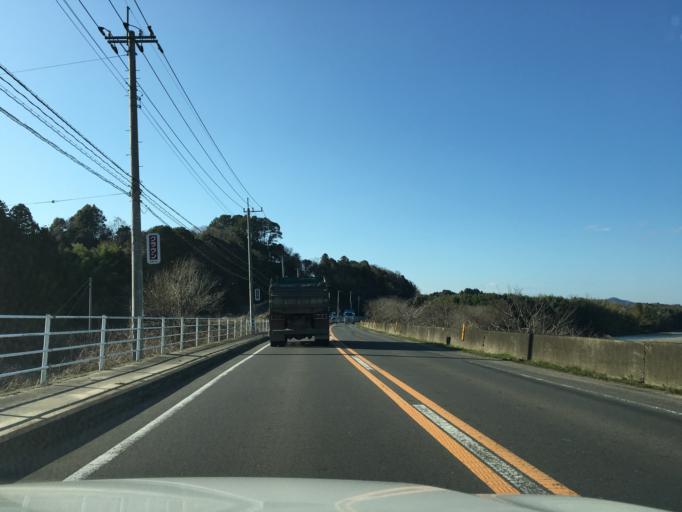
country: JP
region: Ibaraki
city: Omiya
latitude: 36.6011
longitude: 140.4025
